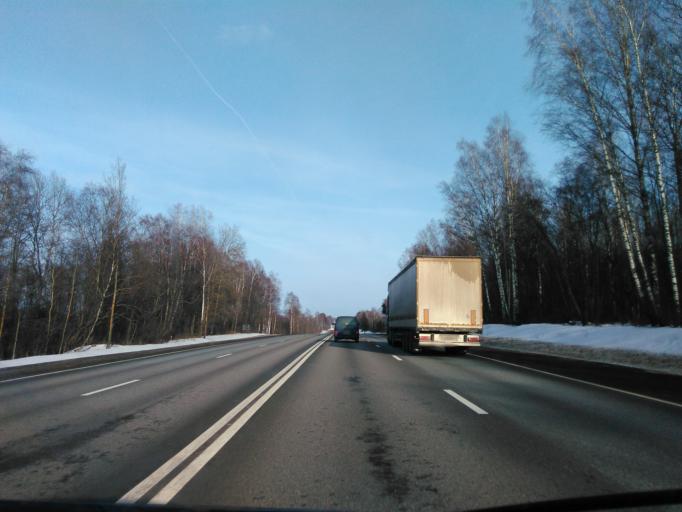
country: RU
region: Smolensk
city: Vyaz'ma
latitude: 55.1899
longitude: 34.0736
